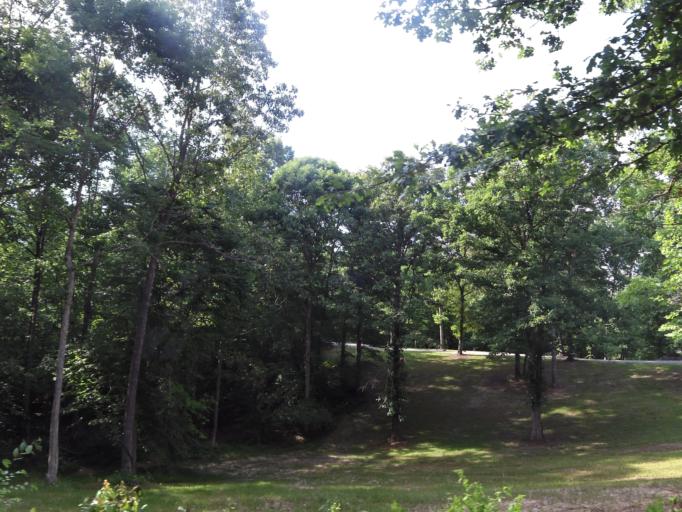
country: US
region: Tennessee
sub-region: Benton County
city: Camden
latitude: 36.0605
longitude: -88.1617
